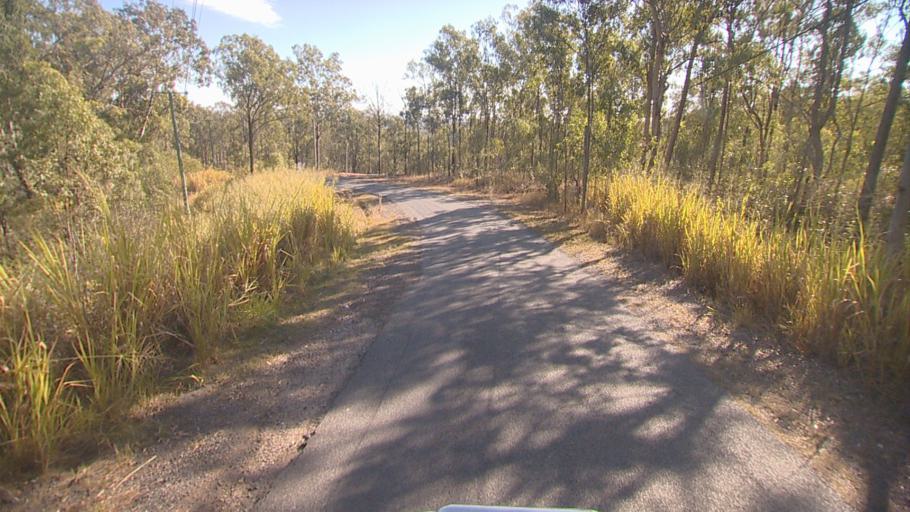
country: AU
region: Queensland
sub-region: Logan
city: Cedar Vale
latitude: -27.8467
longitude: 153.0731
